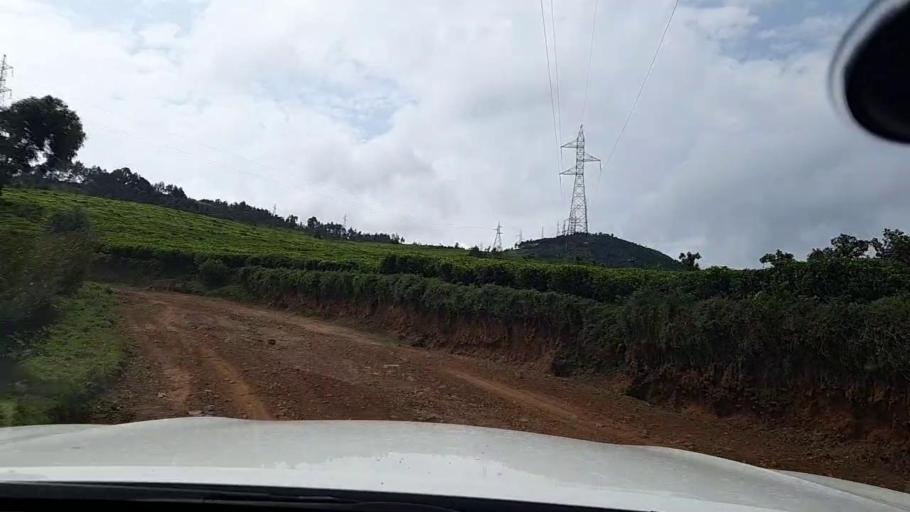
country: RW
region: Western Province
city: Kibuye
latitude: -2.1363
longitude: 29.3754
